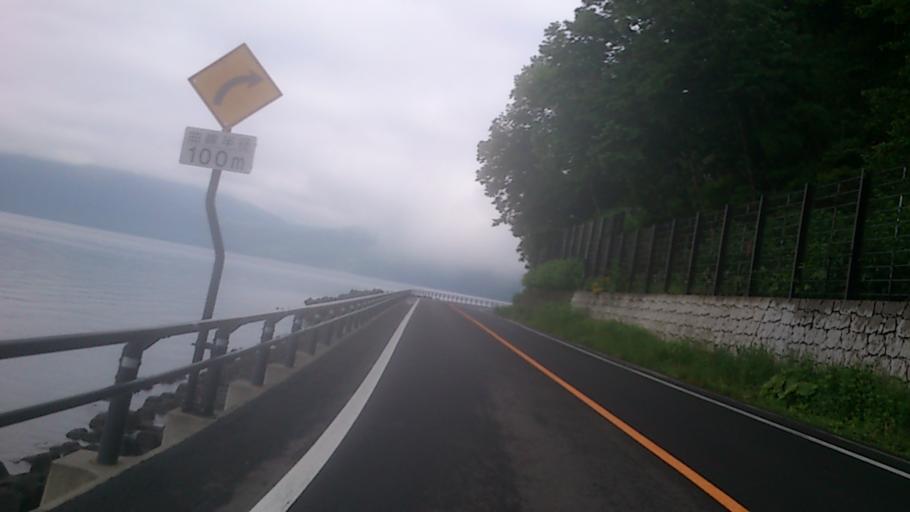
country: JP
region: Hokkaido
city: Shiraoi
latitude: 42.7827
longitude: 141.3849
